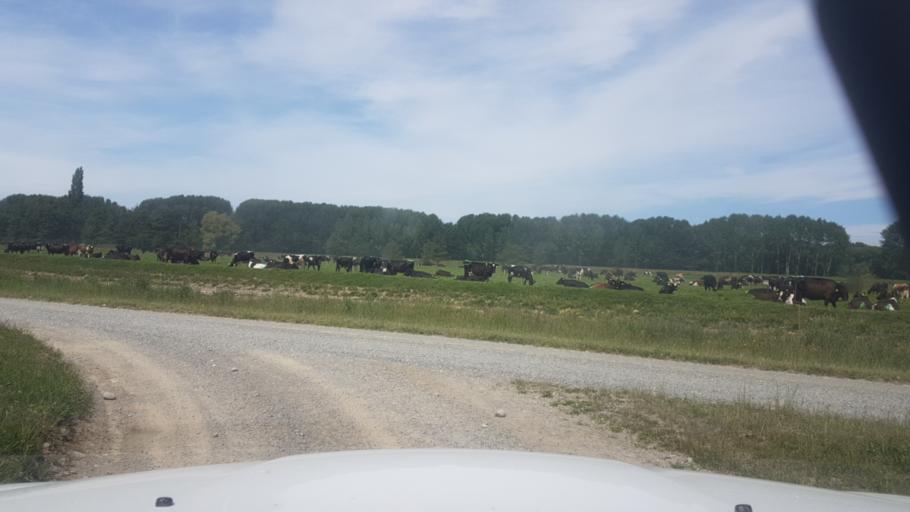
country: NZ
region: Canterbury
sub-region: Timaru District
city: Pleasant Point
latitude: -44.2233
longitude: 171.1189
